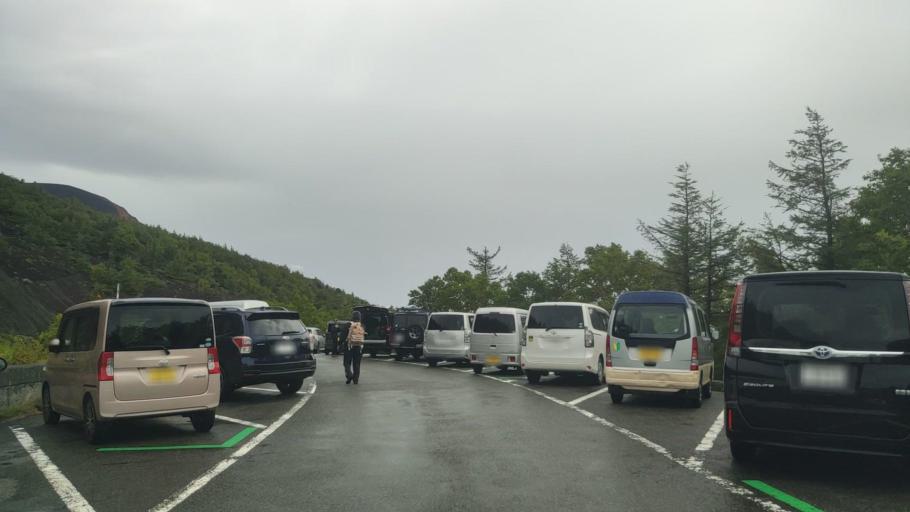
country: JP
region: Yamanashi
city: Fujikawaguchiko
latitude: 35.3363
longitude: 138.7349
